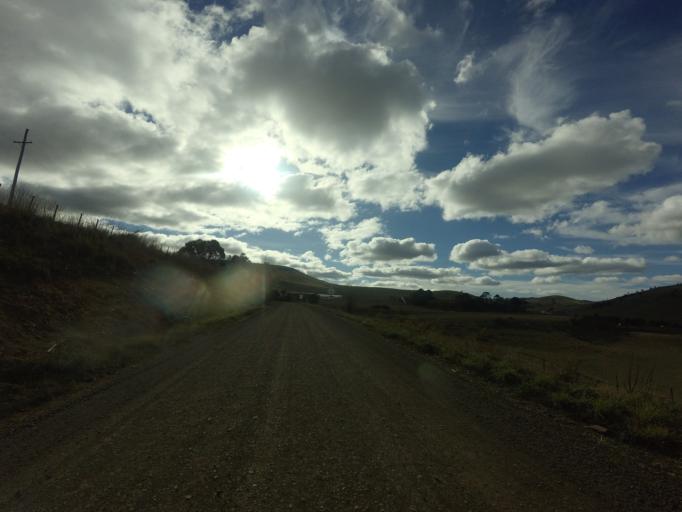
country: AU
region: Tasmania
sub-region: Brighton
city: Bridgewater
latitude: -42.4452
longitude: 147.2279
